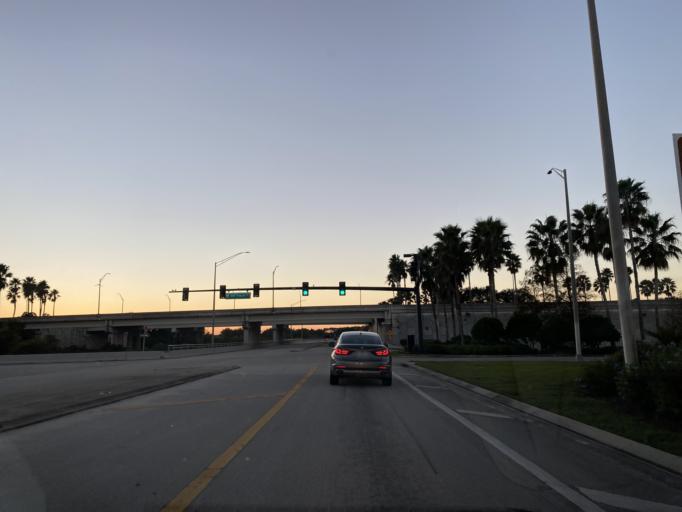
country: US
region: Florida
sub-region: Orange County
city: Meadow Woods
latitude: 28.3972
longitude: -81.3087
